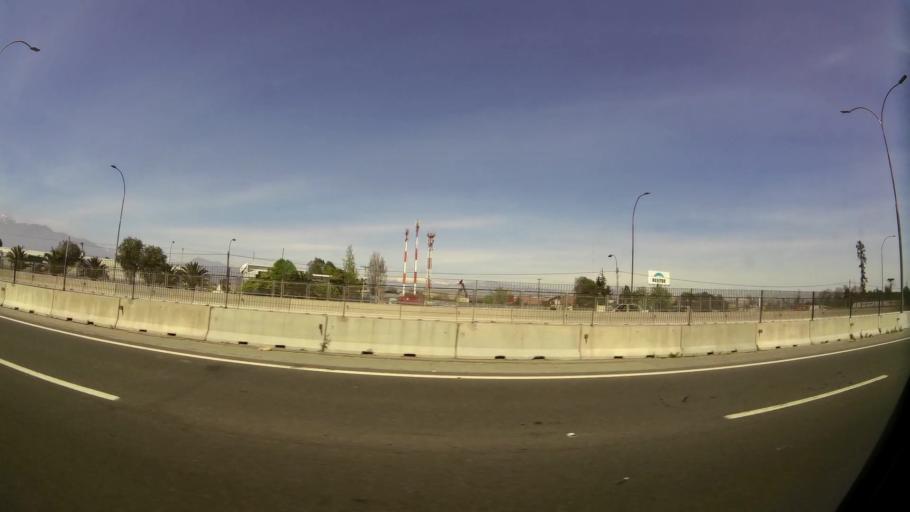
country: CL
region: Santiago Metropolitan
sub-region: Provincia de Maipo
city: San Bernardo
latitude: -33.5419
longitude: -70.6876
